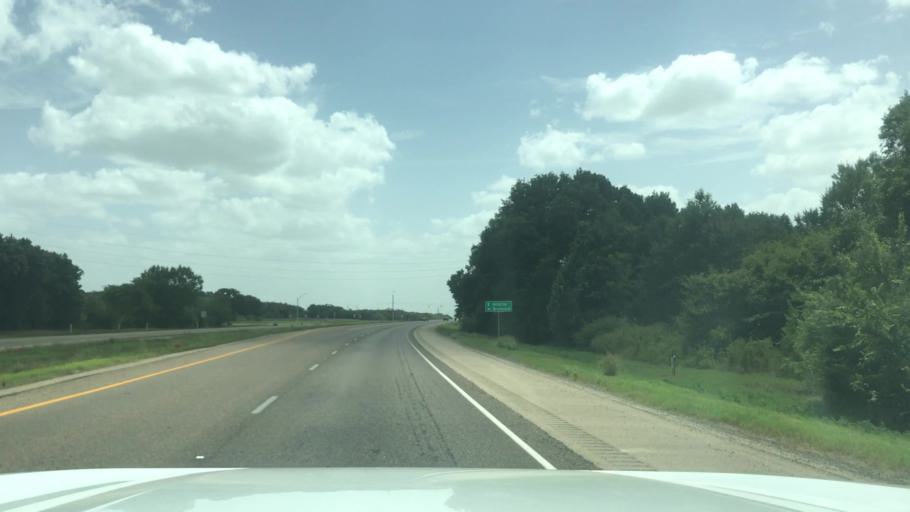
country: US
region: Texas
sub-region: Robertson County
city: Calvert
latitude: 31.1177
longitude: -96.7121
